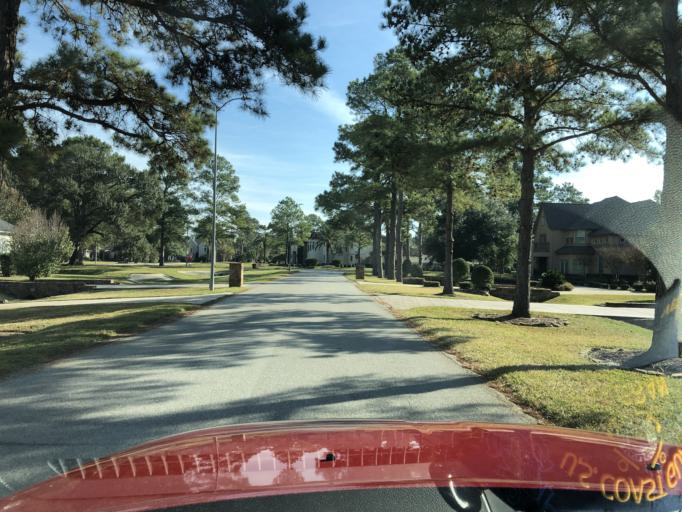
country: US
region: Texas
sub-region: Harris County
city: Tomball
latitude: 30.0396
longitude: -95.5586
